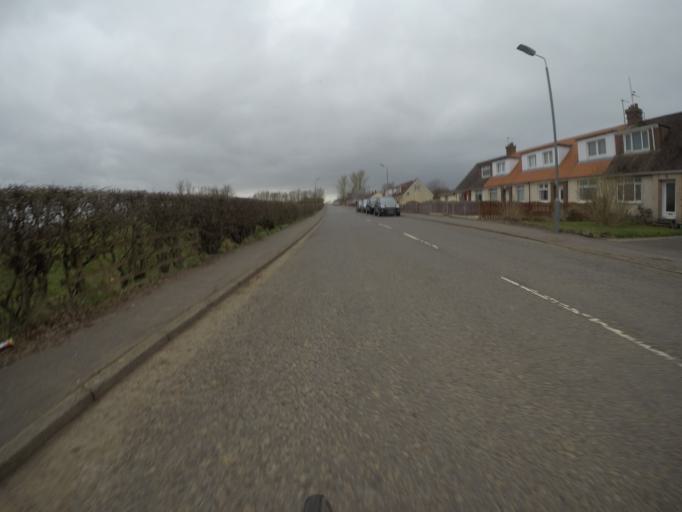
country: GB
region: Scotland
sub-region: North Ayrshire
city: Springside
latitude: 55.6163
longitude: -4.5900
